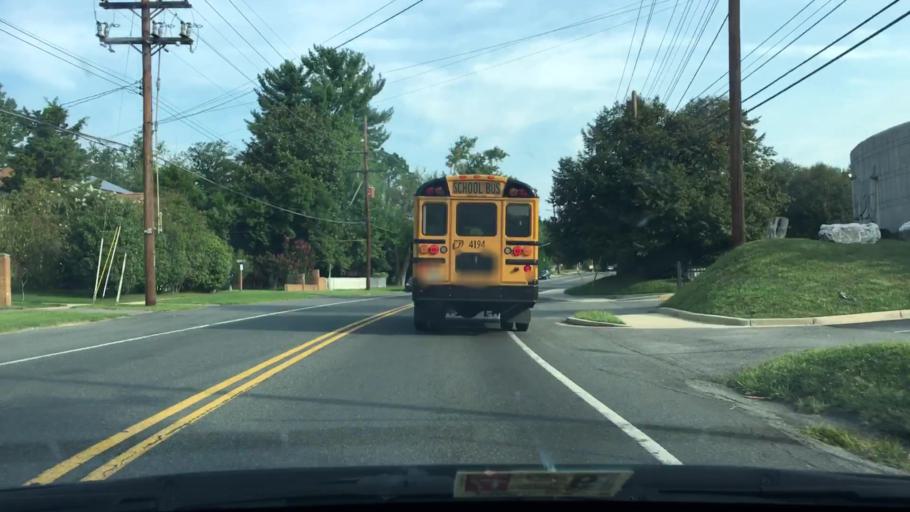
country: US
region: Maryland
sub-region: Montgomery County
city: Rockville
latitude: 39.0505
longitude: -77.1640
